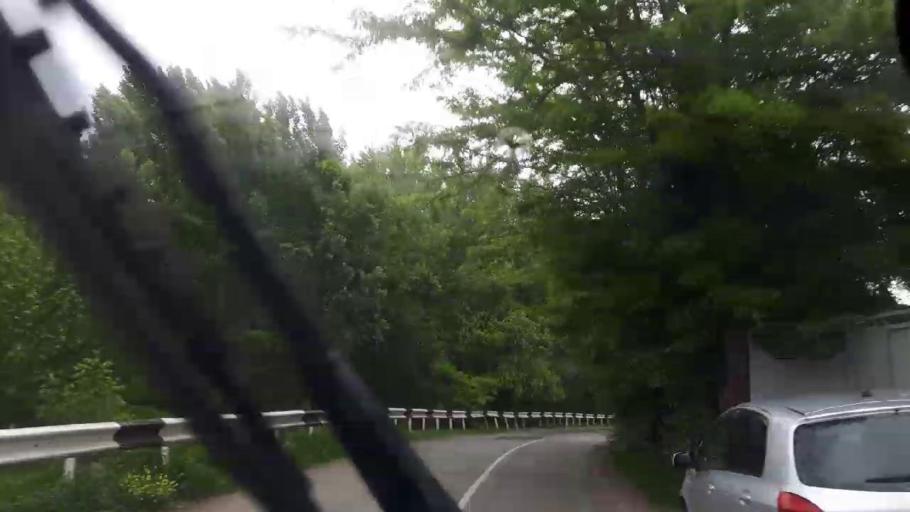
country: GE
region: Shida Kartli
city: Gori
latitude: 41.9659
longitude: 44.2185
